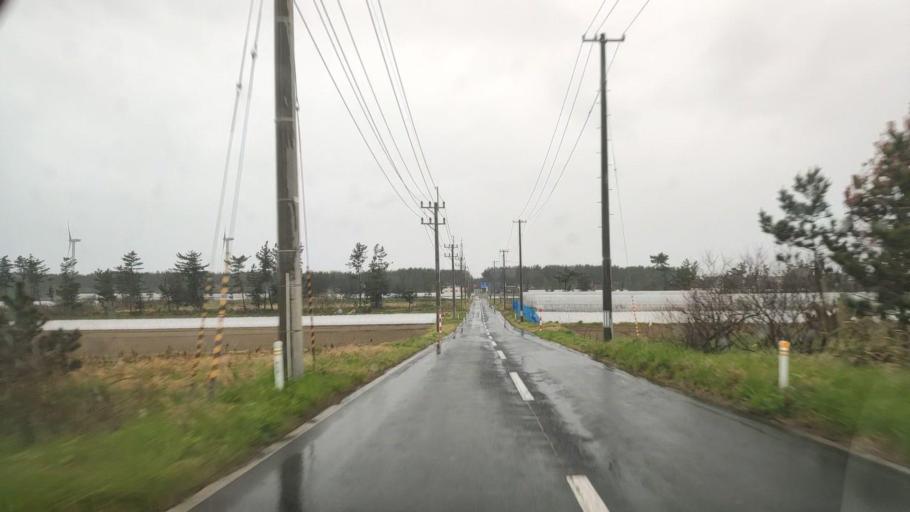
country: JP
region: Akita
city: Noshiromachi
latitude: 40.0966
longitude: 139.9702
